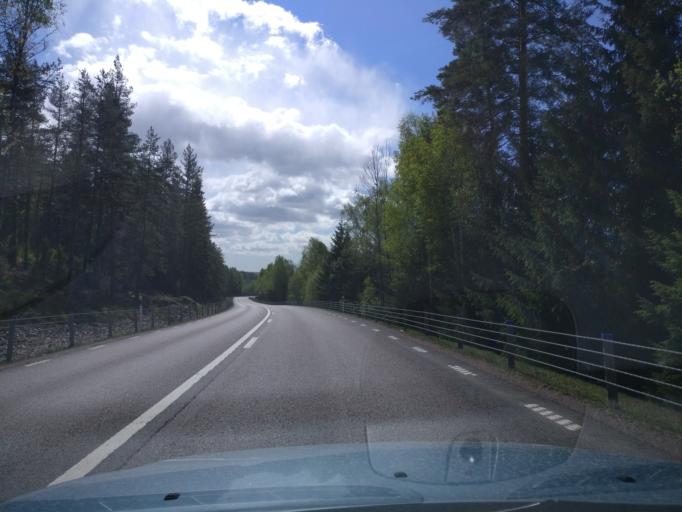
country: SE
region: Vaermland
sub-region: Karlstads Kommun
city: Molkom
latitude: 59.5779
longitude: 13.6676
